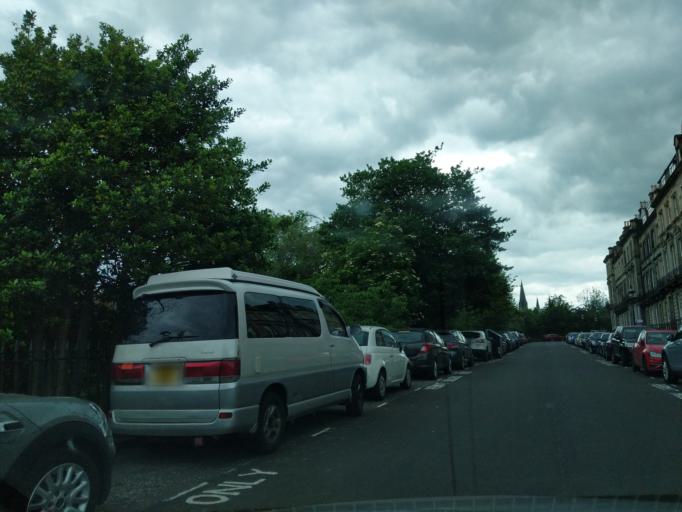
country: GB
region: Scotland
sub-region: Edinburgh
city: Edinburgh
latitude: 55.9552
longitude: -3.2130
